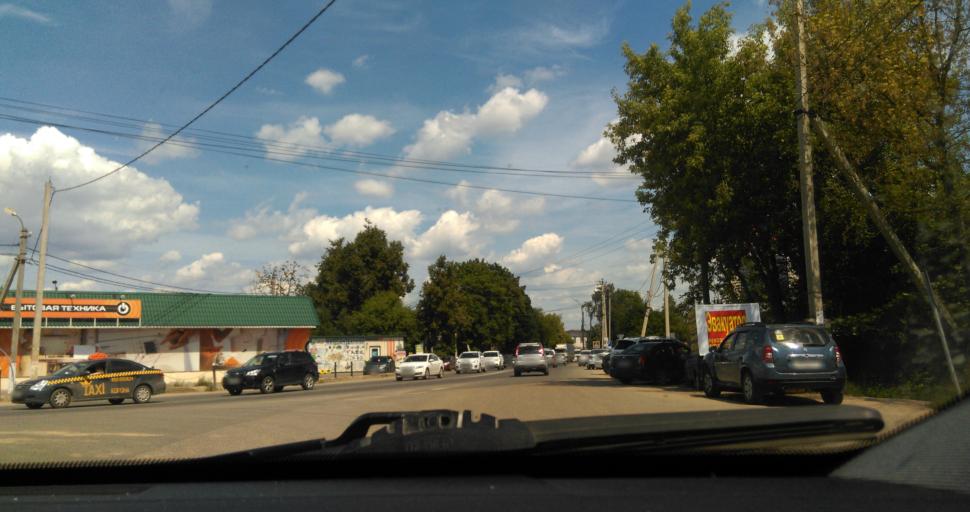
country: RU
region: Moskovskaya
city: Tuchkovo
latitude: 55.6001
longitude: 36.4718
